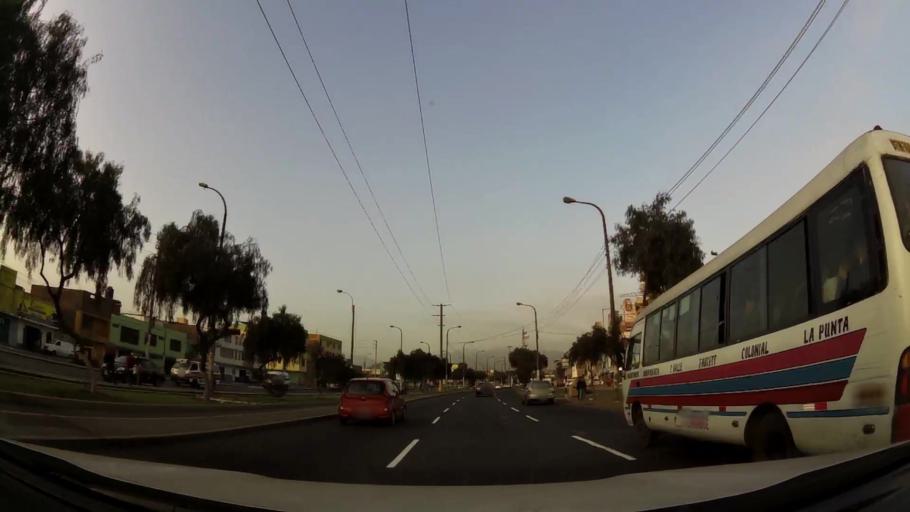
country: PE
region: Callao
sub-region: Callao
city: Callao
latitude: -12.0124
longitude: -77.0926
